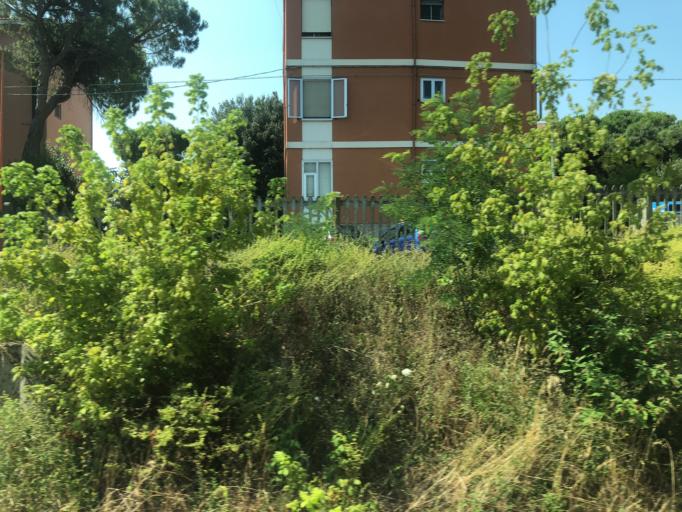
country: IT
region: Emilia-Romagna
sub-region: Forli-Cesena
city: Cesena
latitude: 44.1436
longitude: 12.2553
